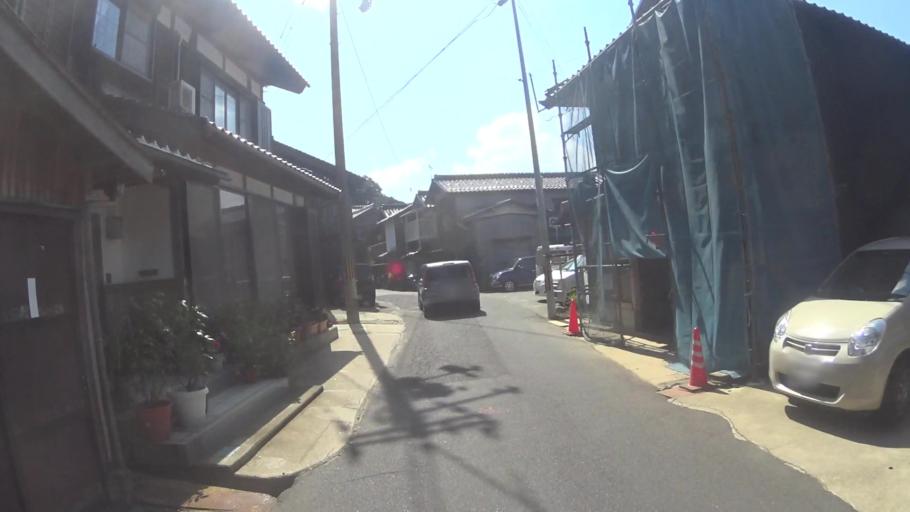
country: JP
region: Kyoto
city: Miyazu
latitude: 35.6680
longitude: 135.2912
